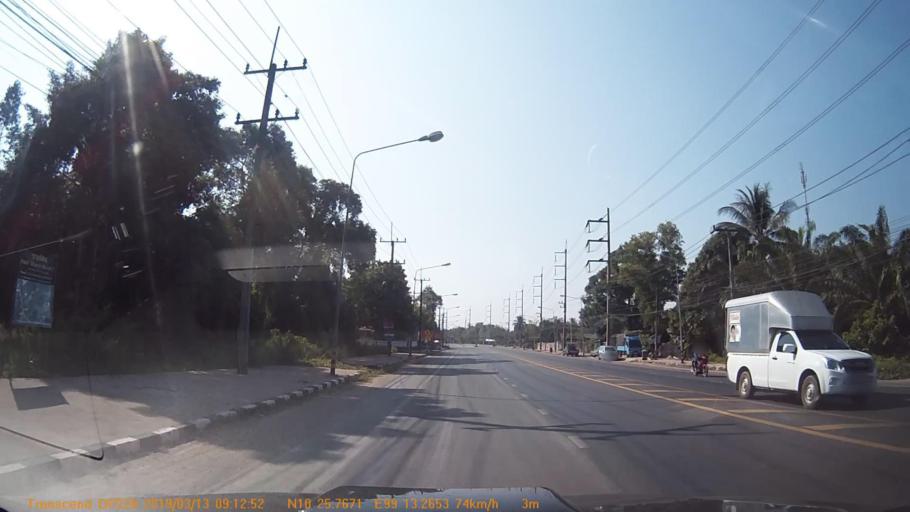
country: TH
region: Chumphon
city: Chumphon
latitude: 10.4292
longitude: 99.2212
